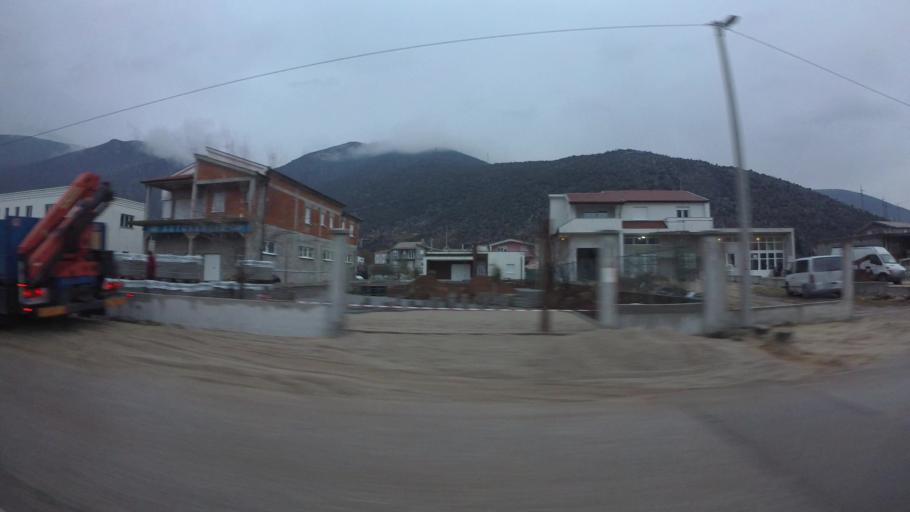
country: BA
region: Federation of Bosnia and Herzegovina
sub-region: Hercegovacko-Bosanski Kanton
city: Mostar
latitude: 43.3661
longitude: 17.8160
